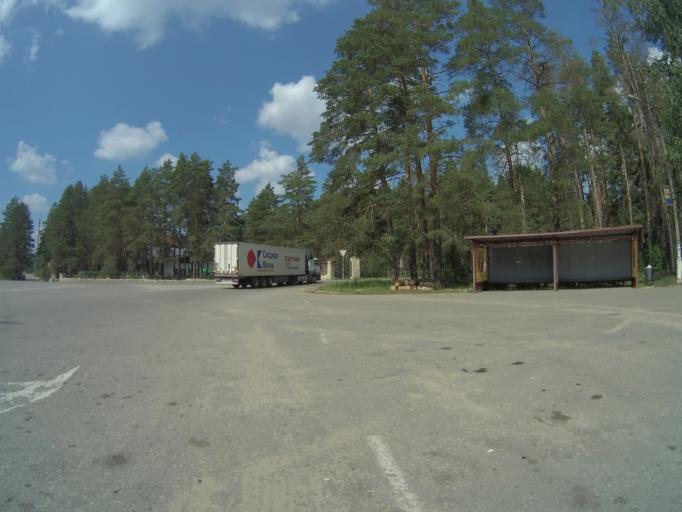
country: RU
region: Vladimir
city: Gus'-Khrustal'nyy
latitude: 55.6325
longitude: 40.6949
